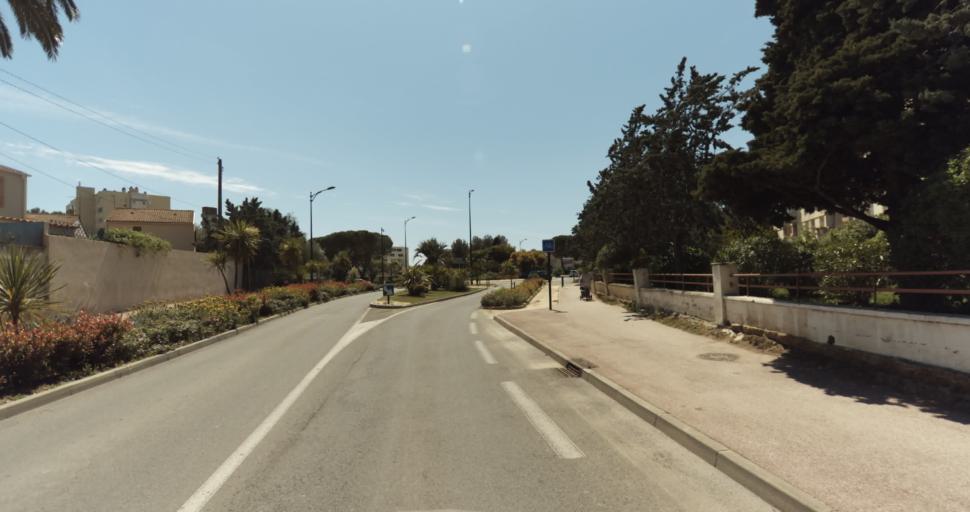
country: FR
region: Provence-Alpes-Cote d'Azur
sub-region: Departement du Var
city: Hyeres
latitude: 43.1254
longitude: 6.1509
